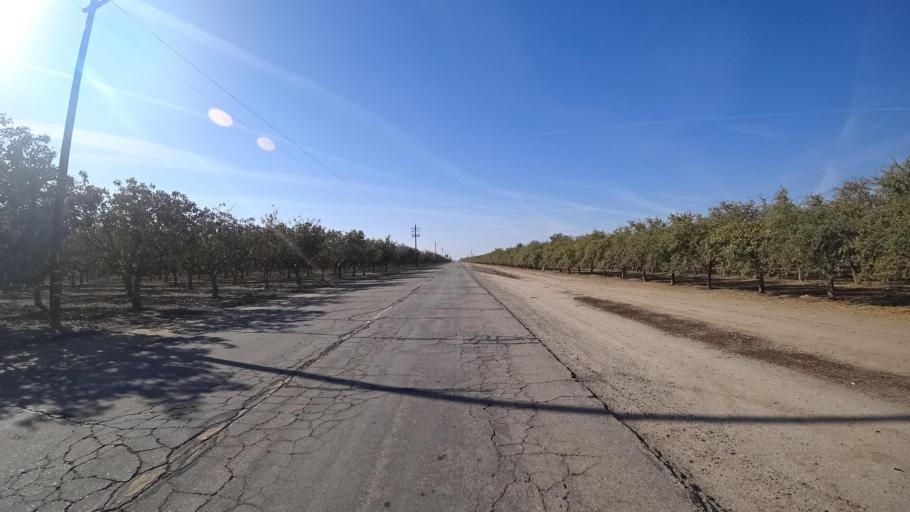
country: US
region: California
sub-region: Kern County
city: Wasco
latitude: 35.6669
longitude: -119.3538
